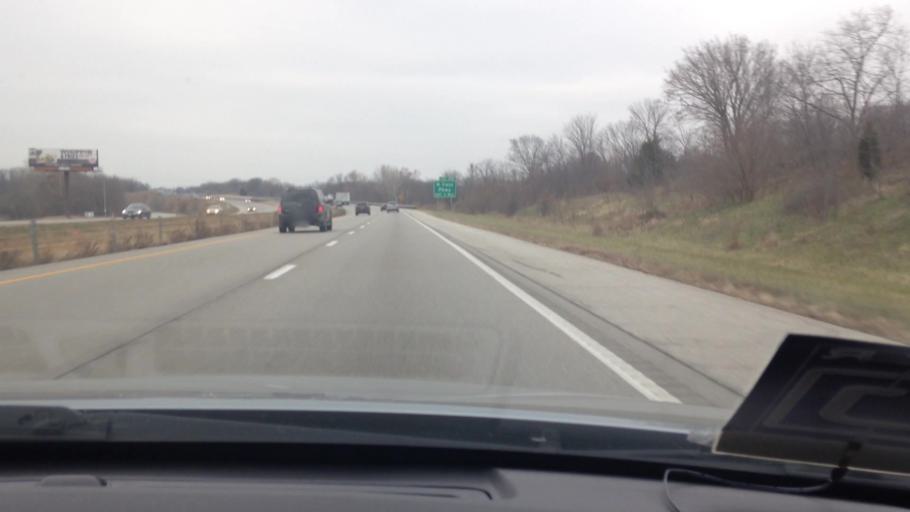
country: US
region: Missouri
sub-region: Cass County
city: Raymore
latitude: 38.7667
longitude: -94.4903
